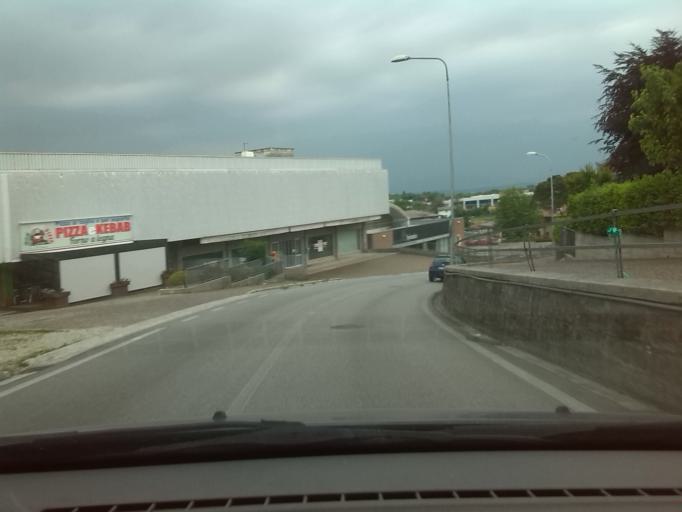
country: IT
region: Friuli Venezia Giulia
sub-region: Provincia di Udine
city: Santo Stefano
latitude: 46.2049
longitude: 13.1236
